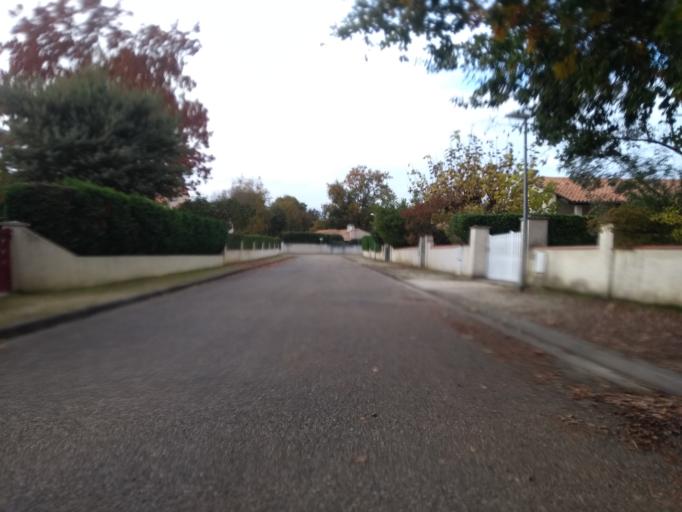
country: FR
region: Aquitaine
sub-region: Departement de la Gironde
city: Canejan
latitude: 44.7648
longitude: -0.6495
